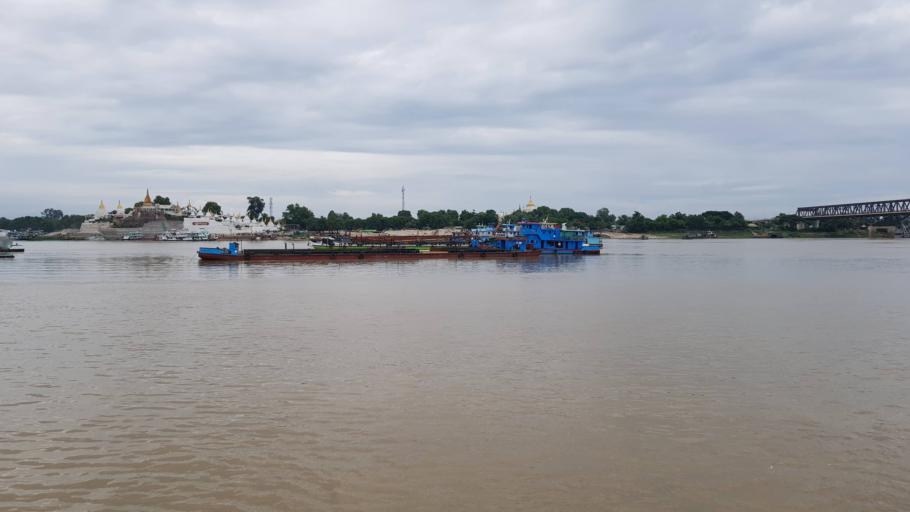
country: MM
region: Sagain
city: Sagaing
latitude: 21.8807
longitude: 95.9968
